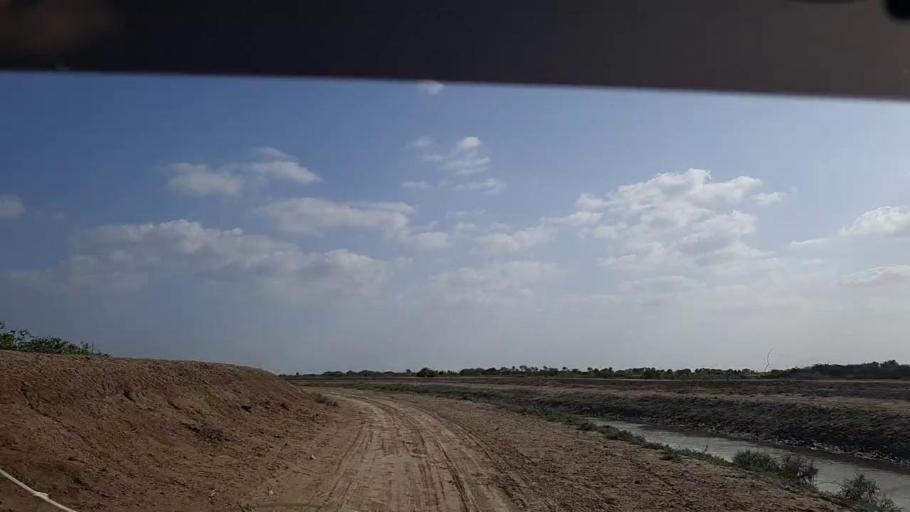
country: PK
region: Sindh
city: Kadhan
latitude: 24.4531
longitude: 68.8580
